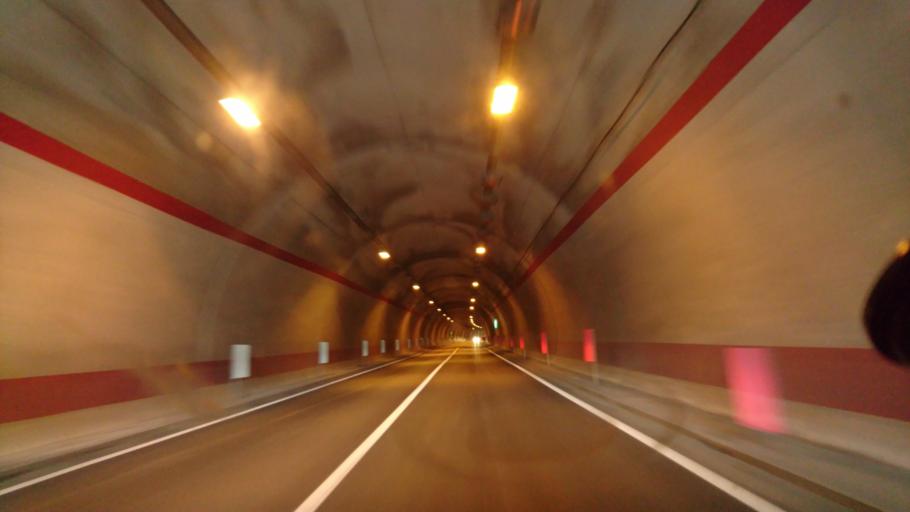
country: IT
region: Liguria
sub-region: Provincia di Savona
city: Carcare
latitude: 44.3477
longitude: 8.3132
